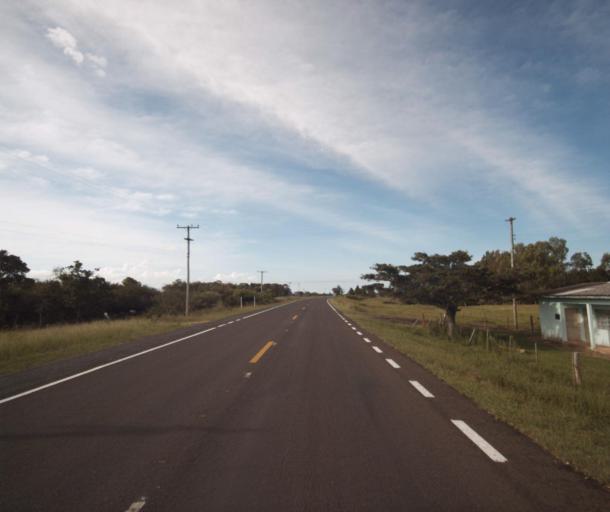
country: BR
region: Rio Grande do Sul
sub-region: Tapes
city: Tapes
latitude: -31.3244
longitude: -51.1250
